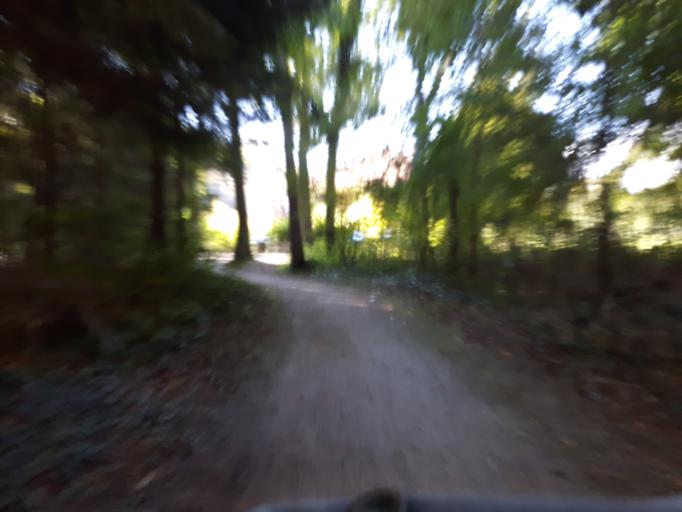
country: NL
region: Utrecht
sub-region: Gemeente Utrechtse Heuvelrug
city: Driebergen-Rijsenburg
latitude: 52.0594
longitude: 5.2808
